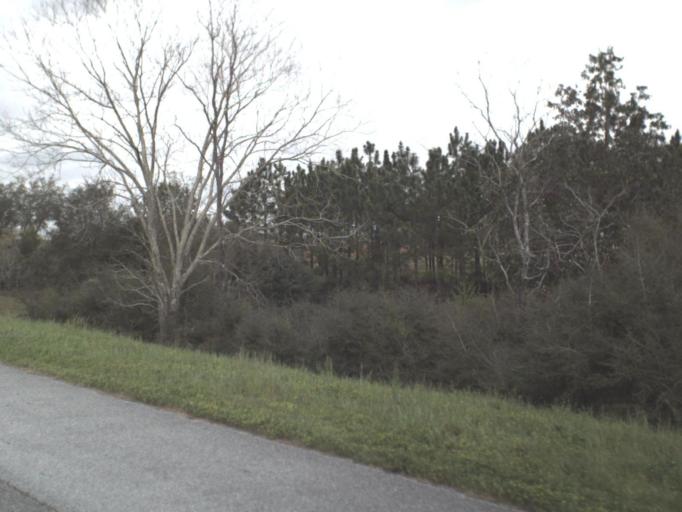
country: US
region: Florida
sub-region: Okaloosa County
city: Crestview
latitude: 30.7180
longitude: -86.4495
